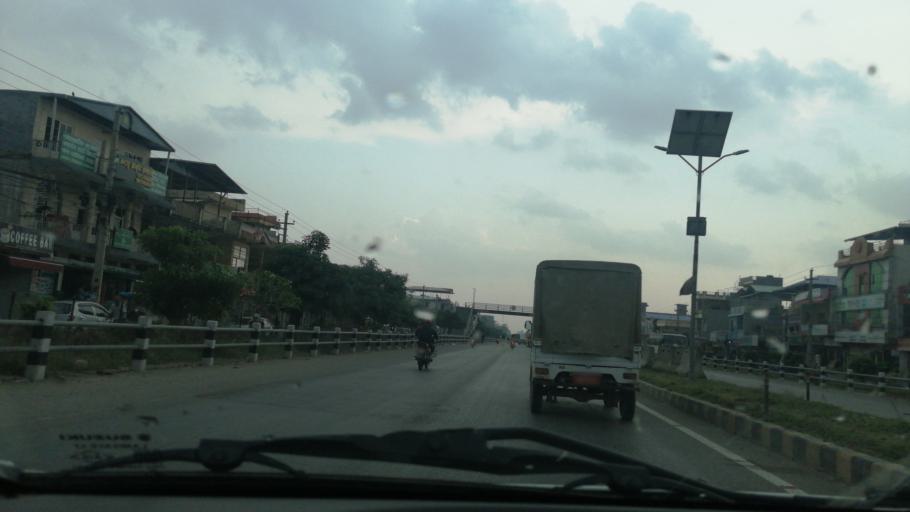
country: NP
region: Western Region
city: Butwal
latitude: 27.6765
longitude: 83.4648
